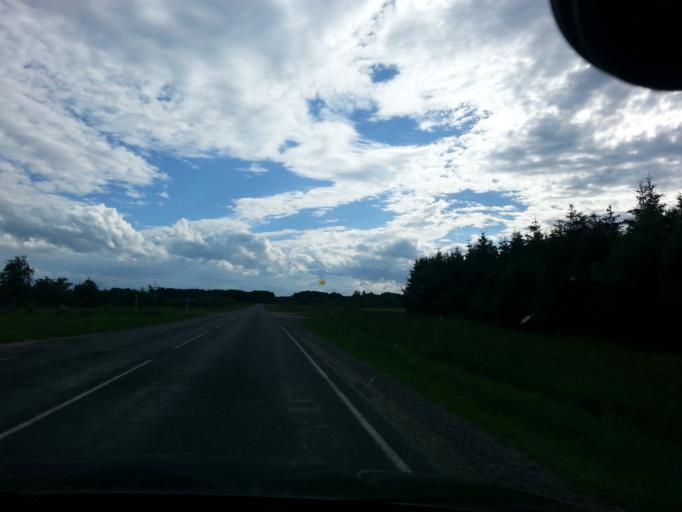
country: BY
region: Grodnenskaya
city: Astravyets
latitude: 54.8050
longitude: 26.1345
